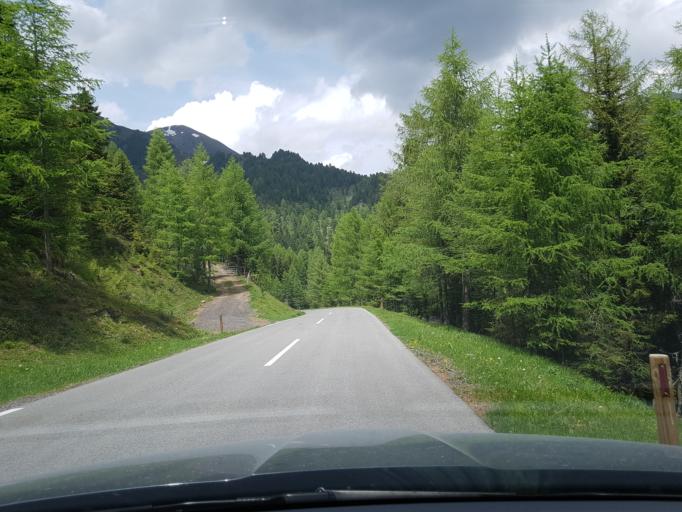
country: AT
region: Carinthia
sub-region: Politischer Bezirk Spittal an der Drau
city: Kleinkirchheim
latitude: 46.8947
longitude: 13.8148
